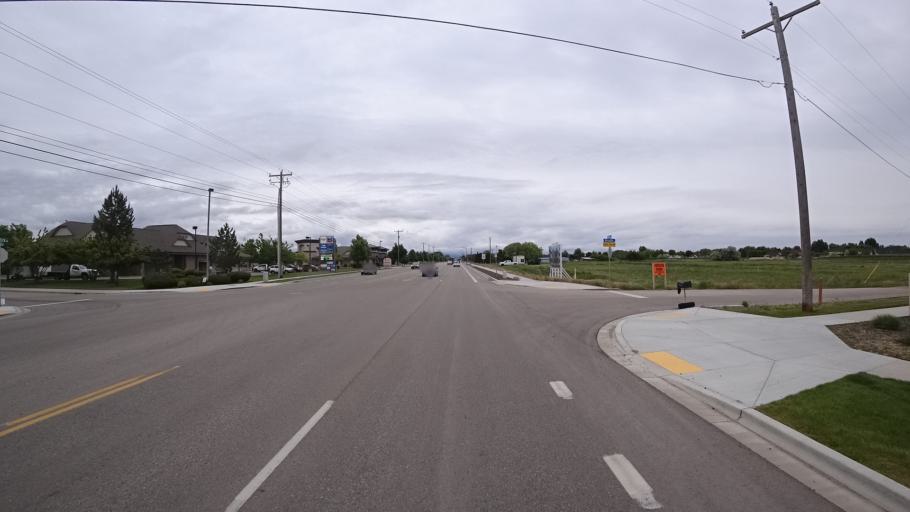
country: US
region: Idaho
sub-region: Ada County
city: Meridian
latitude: 43.6337
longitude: -116.4039
